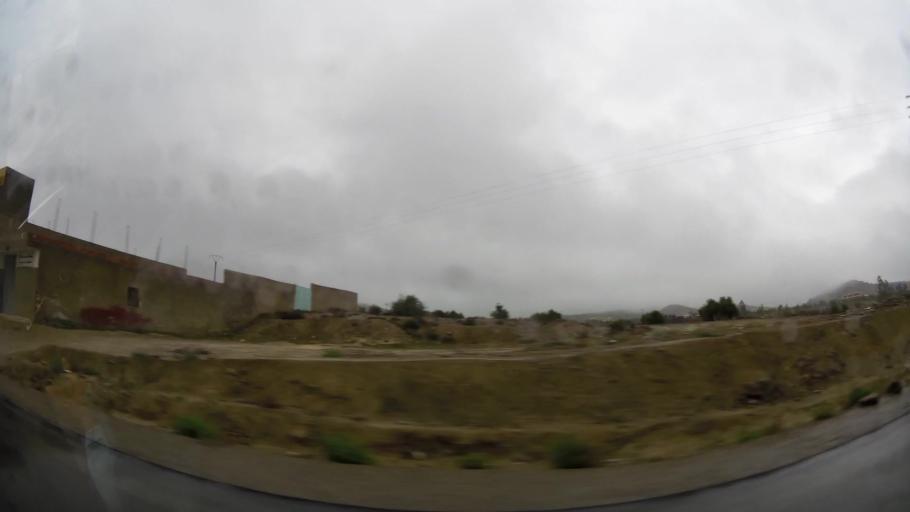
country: MA
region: Taza-Al Hoceima-Taounate
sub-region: Taza
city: Aknoul
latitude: 34.8210
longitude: -3.7259
